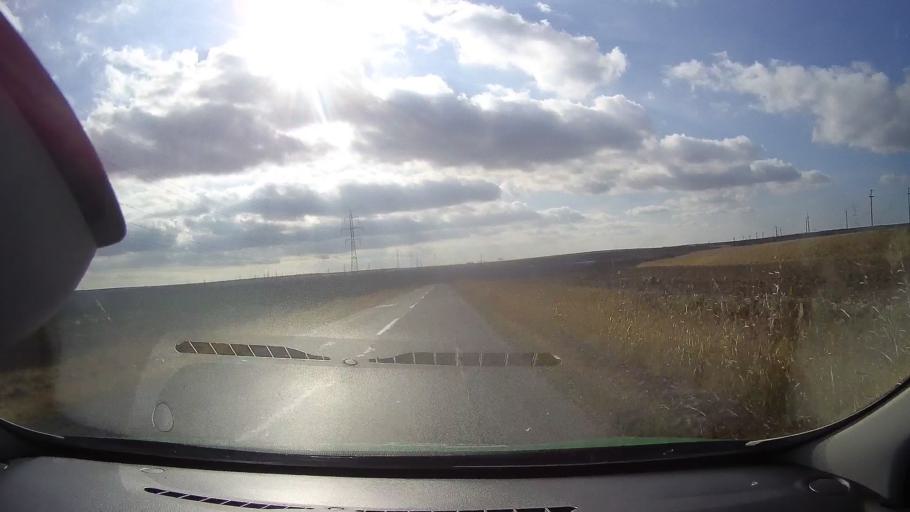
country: RO
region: Constanta
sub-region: Comuna Sacele
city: Sacele
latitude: 44.5014
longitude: 28.6618
